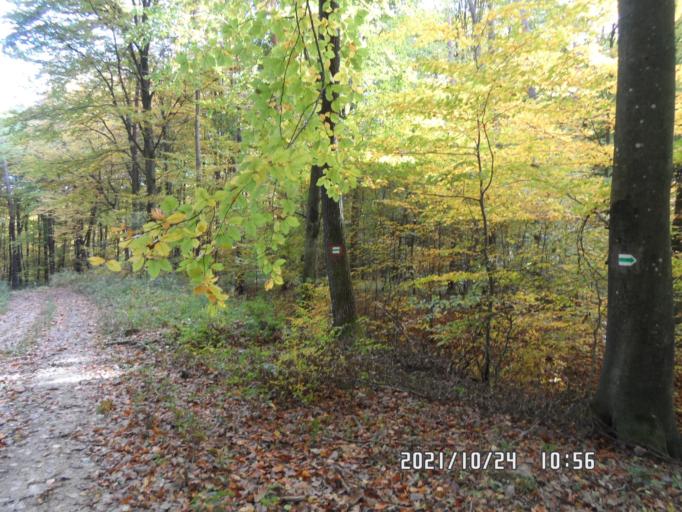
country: SI
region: Hodos-Hodos
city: Hodos
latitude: 46.8093
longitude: 16.3450
